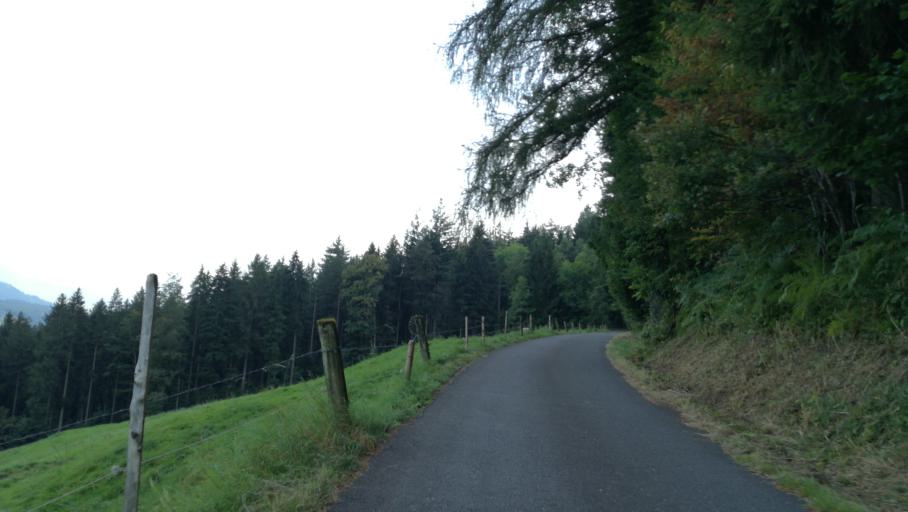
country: CH
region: Zug
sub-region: Zug
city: Zug
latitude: 47.1523
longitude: 8.5493
